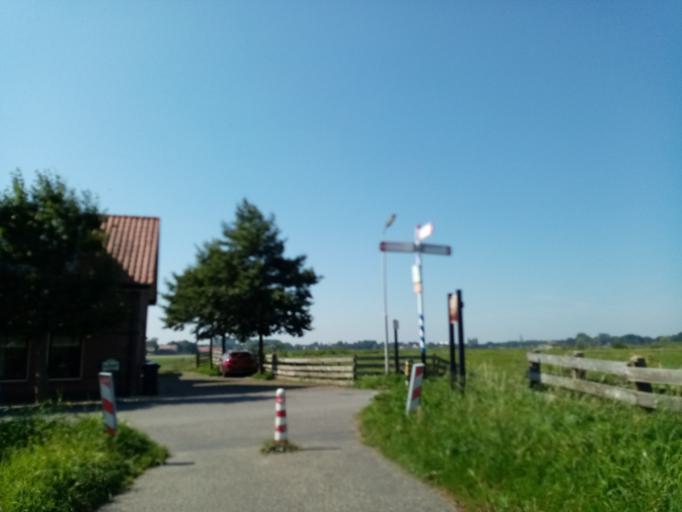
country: NL
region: South Holland
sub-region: Gemeente Teylingen
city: Sassenheim
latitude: 52.2284
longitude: 4.5502
